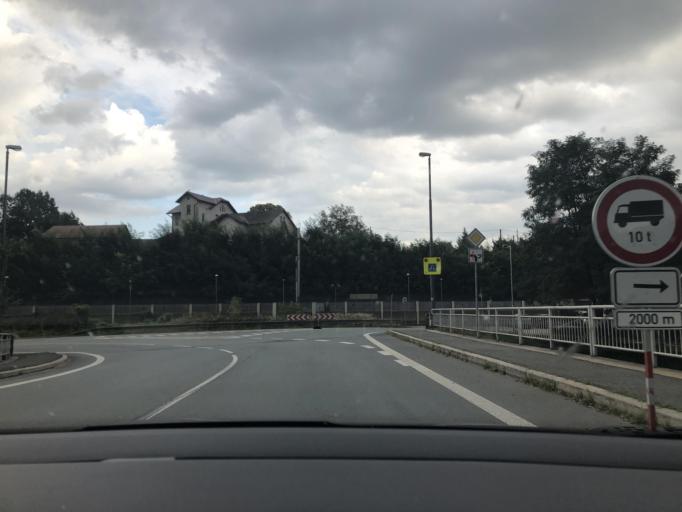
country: CZ
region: Central Bohemia
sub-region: Okres Kolin
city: Tynec nad Labem
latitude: 50.0385
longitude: 15.3592
